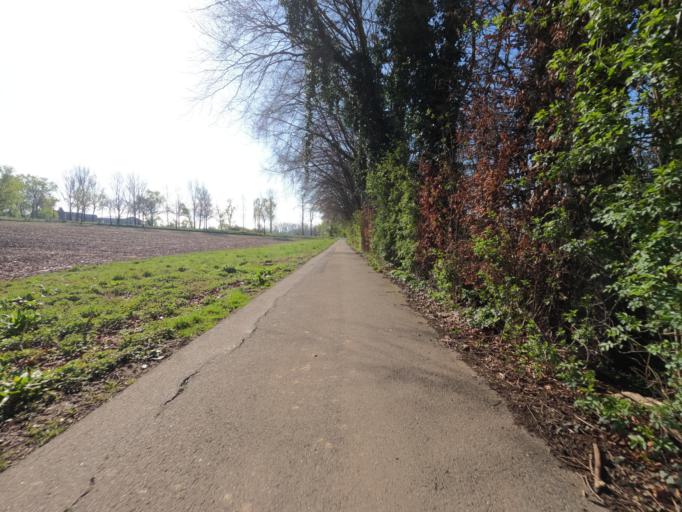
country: DE
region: North Rhine-Westphalia
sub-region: Regierungsbezirk Koln
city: Linnich
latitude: 50.9841
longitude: 6.2915
